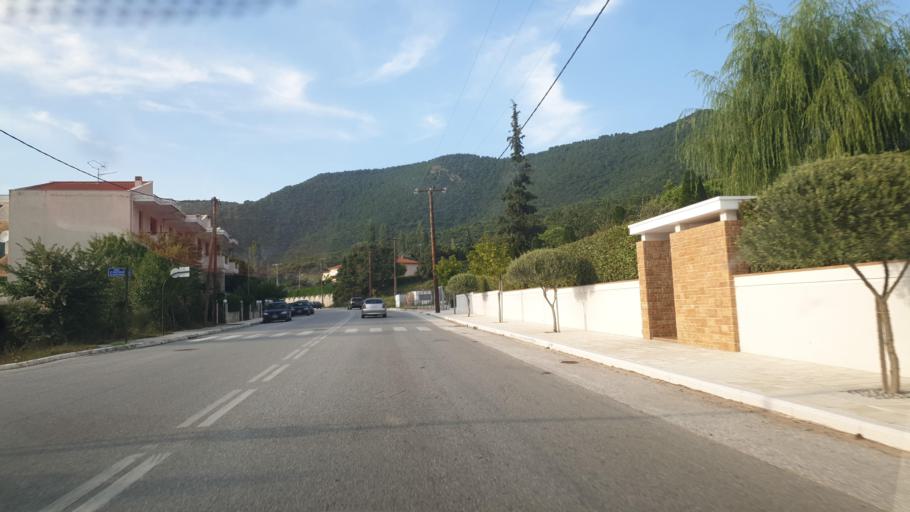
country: GR
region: Central Macedonia
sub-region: Nomos Chalkidikis
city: Polygyros
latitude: 40.3789
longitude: 23.4515
